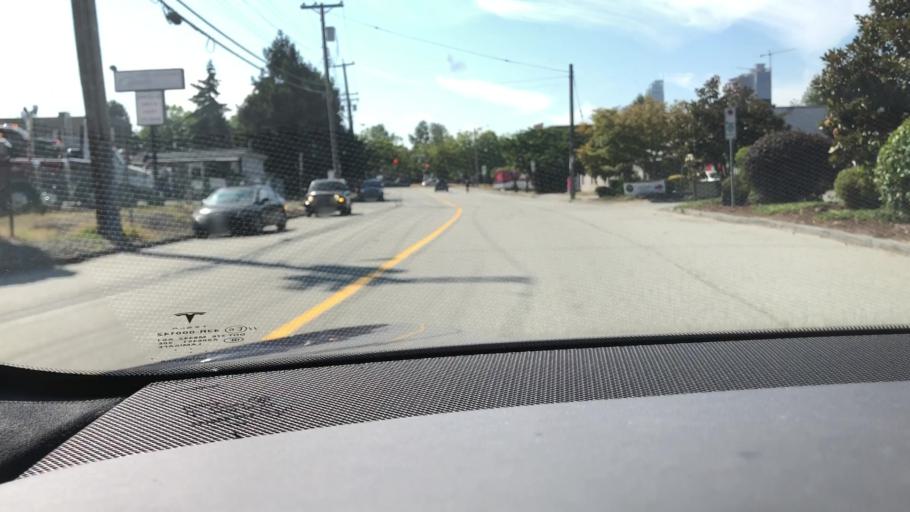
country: CA
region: British Columbia
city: Burnaby
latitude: 49.2593
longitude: -122.9807
